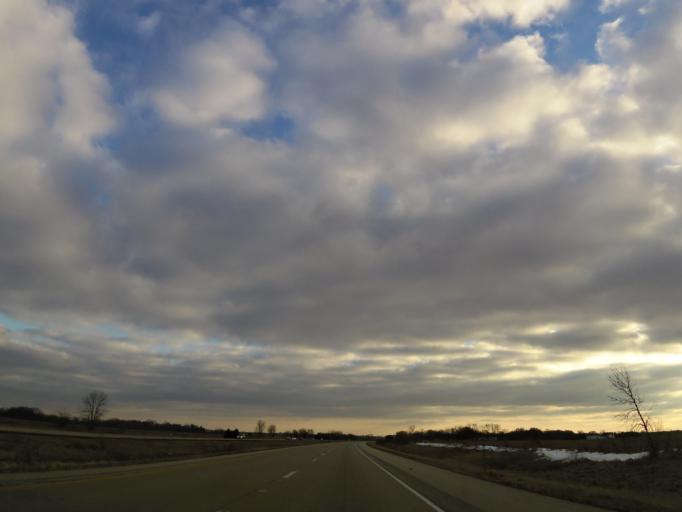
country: US
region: Illinois
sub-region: LaSalle County
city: Mendota
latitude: 41.4989
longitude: -89.0496
